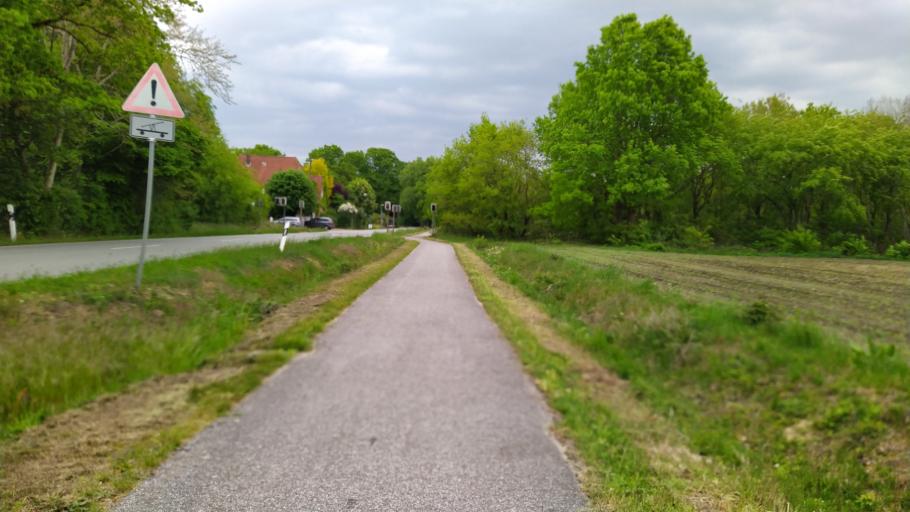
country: DE
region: Lower Saxony
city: Ostereistedt
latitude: 53.2704
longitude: 9.2001
